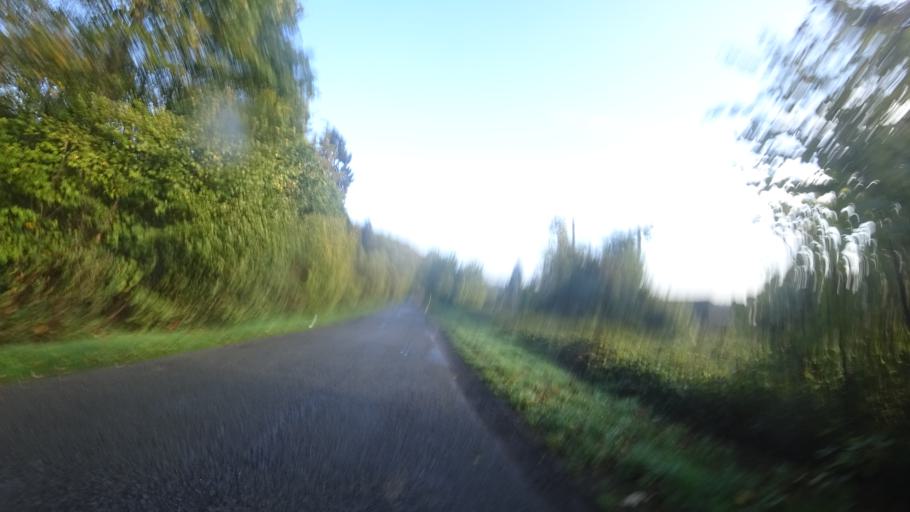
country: BE
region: Wallonia
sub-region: Province de Namur
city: Floreffe
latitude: 50.4498
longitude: 4.7916
